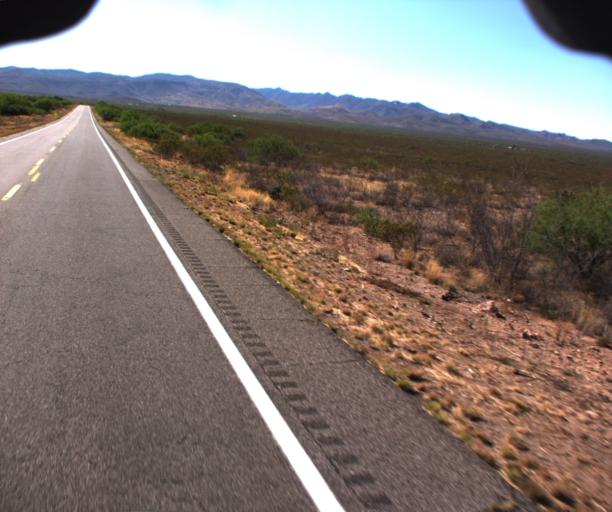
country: US
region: Arizona
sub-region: Cochise County
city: Tombstone
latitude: 31.5845
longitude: -110.0376
